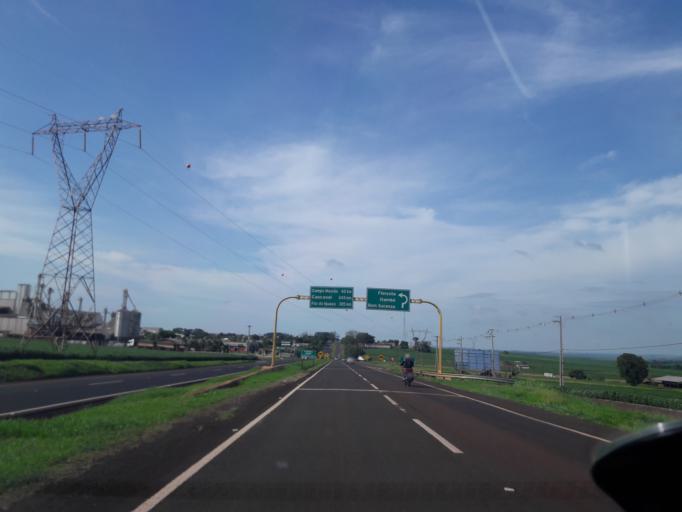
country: BR
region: Parana
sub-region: Paicandu
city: Paicandu
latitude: -23.6021
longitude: -52.0817
